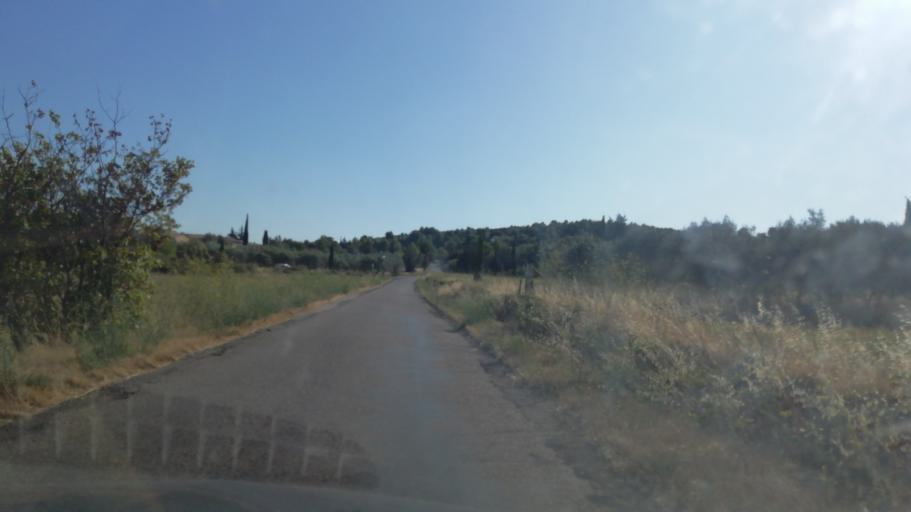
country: FR
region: Languedoc-Roussillon
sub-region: Departement de l'Herault
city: Nebian
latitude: 43.6126
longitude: 3.4364
